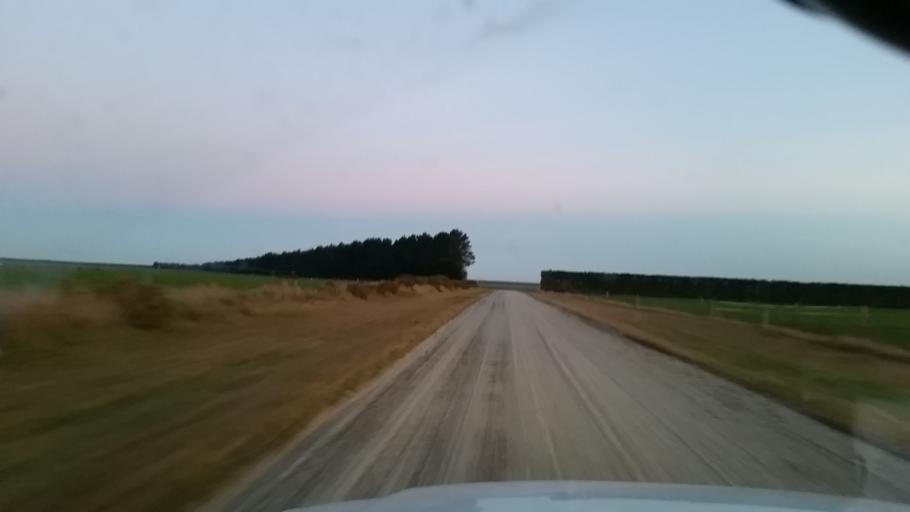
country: NZ
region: Canterbury
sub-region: Ashburton District
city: Tinwald
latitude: -43.9438
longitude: 171.6106
